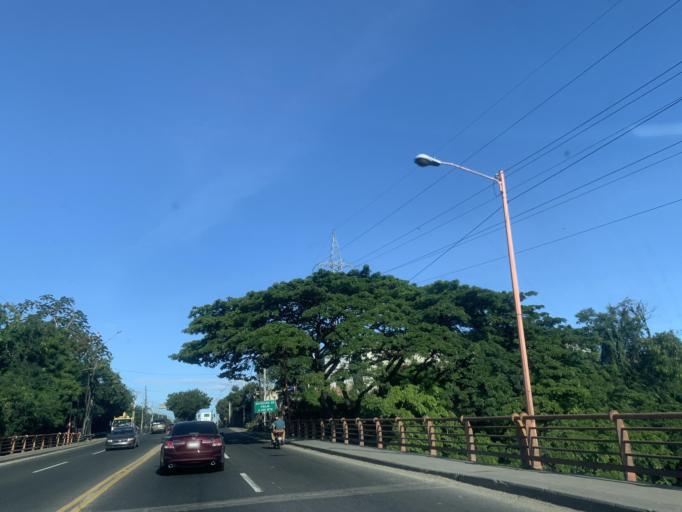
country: DO
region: San Cristobal
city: El Carril
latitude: 18.4313
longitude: -70.0058
